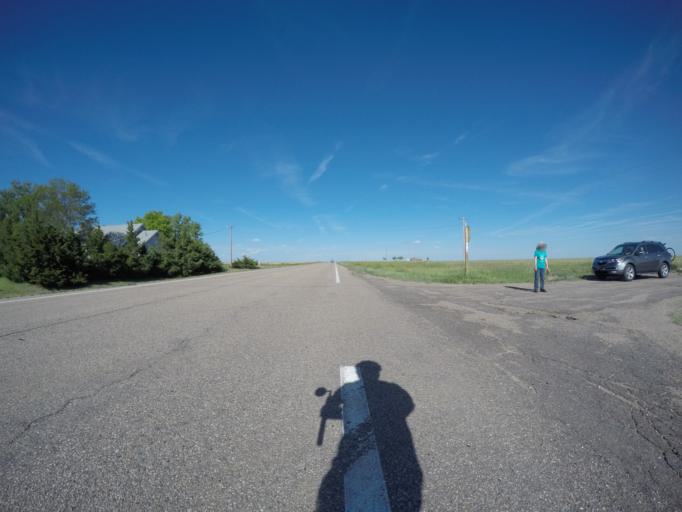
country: US
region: Kansas
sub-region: Cheyenne County
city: Saint Francis
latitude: 39.7565
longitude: -101.9937
